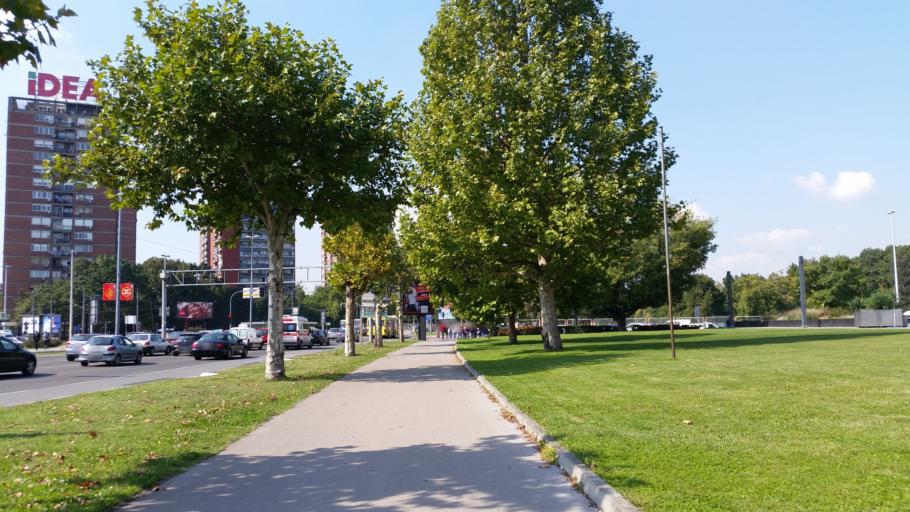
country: RS
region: Central Serbia
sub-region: Belgrade
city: Novi Beograd
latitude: 44.8147
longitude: 20.4360
